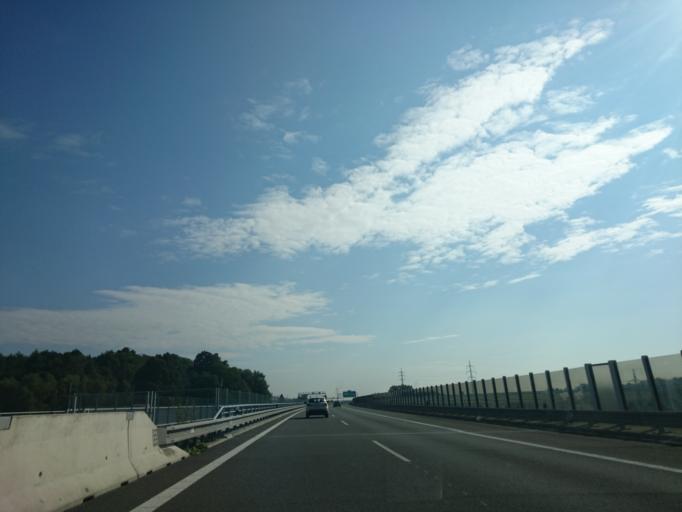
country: CZ
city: Klimkovice
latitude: 49.7965
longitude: 18.1253
